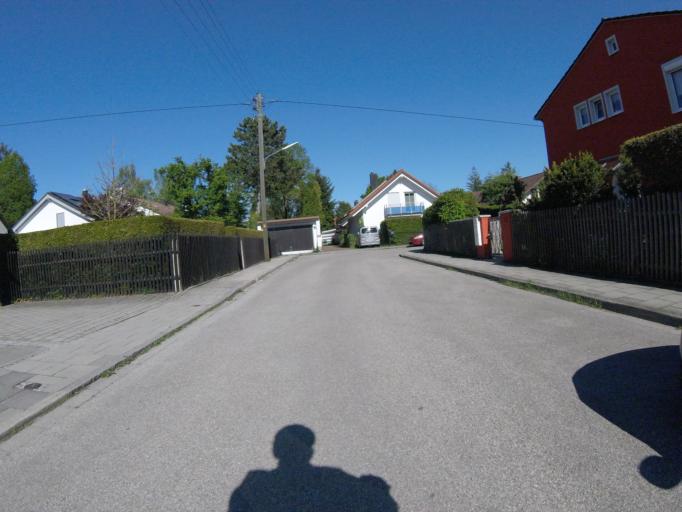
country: DE
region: Bavaria
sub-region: Upper Bavaria
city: Ottobrunn
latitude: 48.0566
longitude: 11.6619
